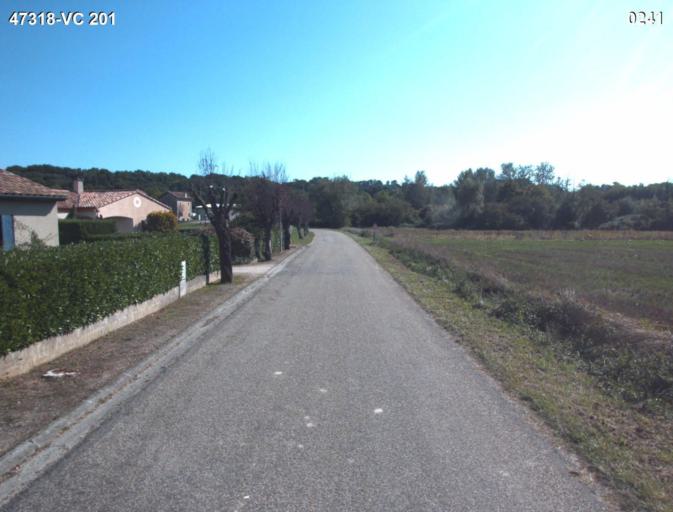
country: FR
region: Aquitaine
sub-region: Departement du Lot-et-Garonne
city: Vianne
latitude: 44.2004
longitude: 0.3213
